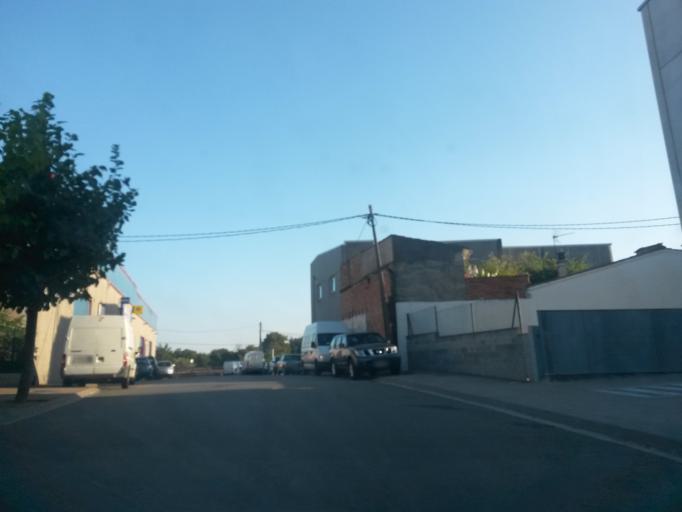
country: ES
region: Catalonia
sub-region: Provincia de Girona
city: Fornells de la Selva
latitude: 41.9321
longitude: 2.7994
